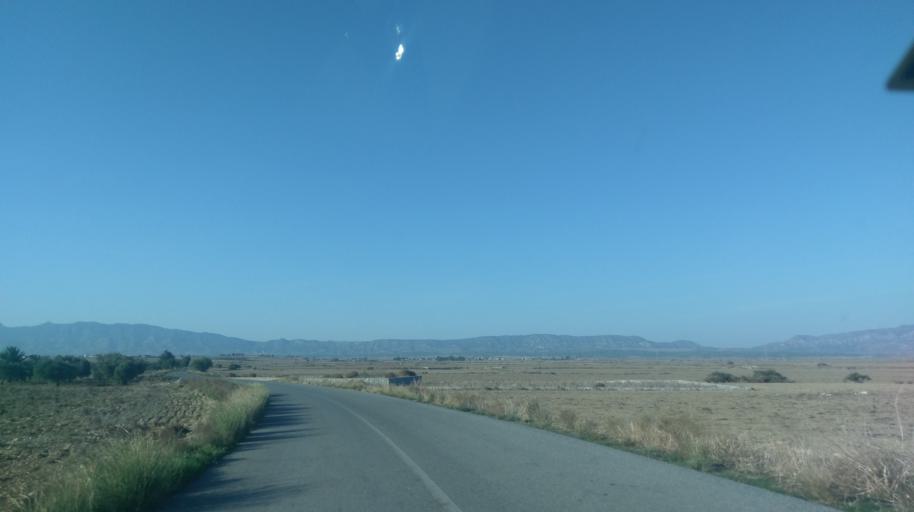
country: CY
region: Ammochostos
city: Lefkonoiko
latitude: 35.2229
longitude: 33.6967
